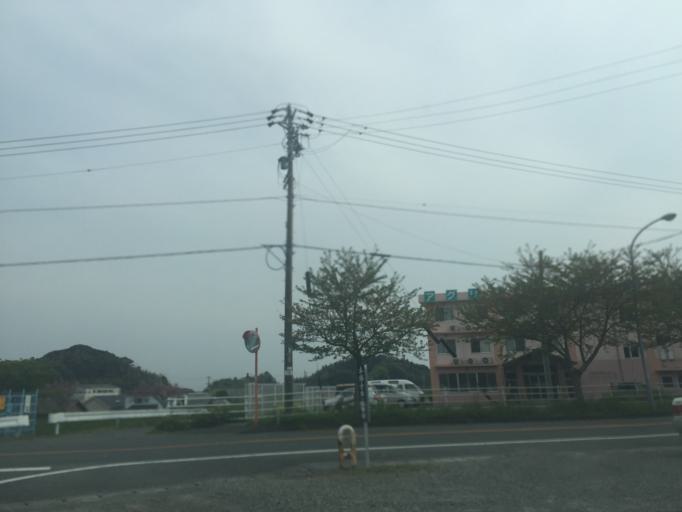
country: JP
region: Shizuoka
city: Kakegawa
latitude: 34.6864
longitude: 138.0535
